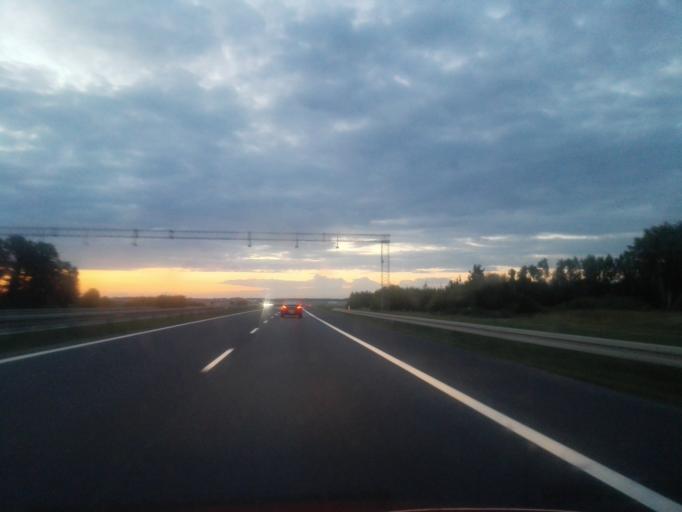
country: PL
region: Lodz Voivodeship
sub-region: Powiat piotrkowski
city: Grabica
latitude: 51.5113
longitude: 19.6019
